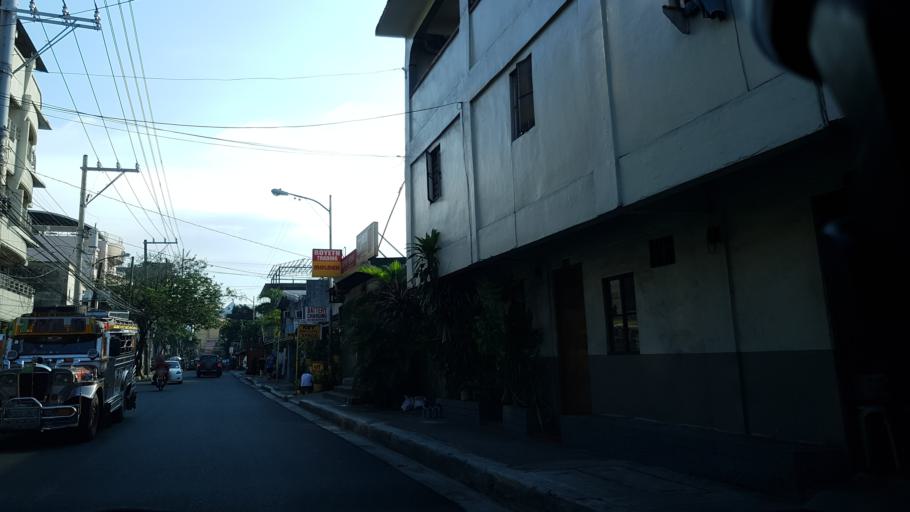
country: PH
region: Metro Manila
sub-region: Mandaluyong
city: Mandaluyong City
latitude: 14.5805
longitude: 121.0288
